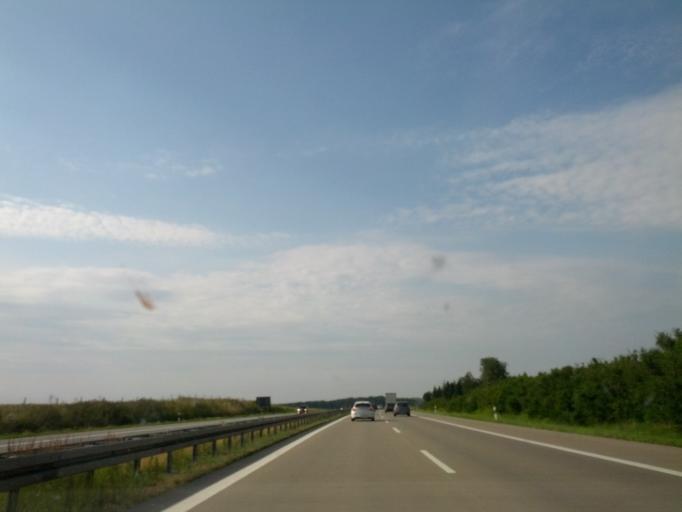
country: DE
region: Mecklenburg-Vorpommern
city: Dummerstorf
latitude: 53.9103
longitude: 12.2409
